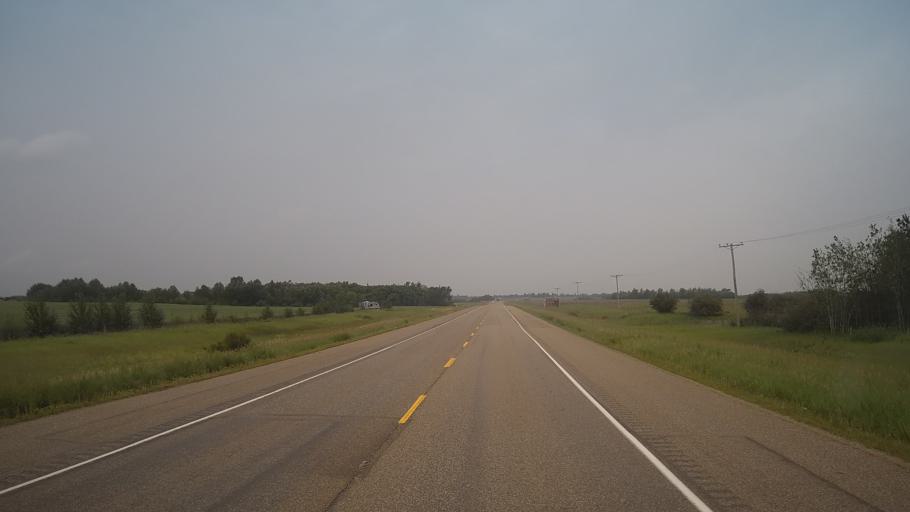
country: CA
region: Saskatchewan
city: Biggar
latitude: 52.0563
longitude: -107.9328
